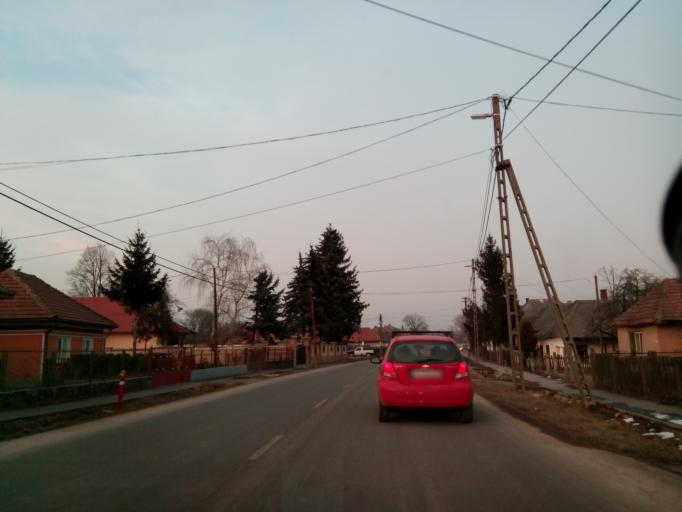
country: HU
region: Borsod-Abauj-Zemplen
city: Gonc
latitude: 48.5019
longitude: 21.2316
